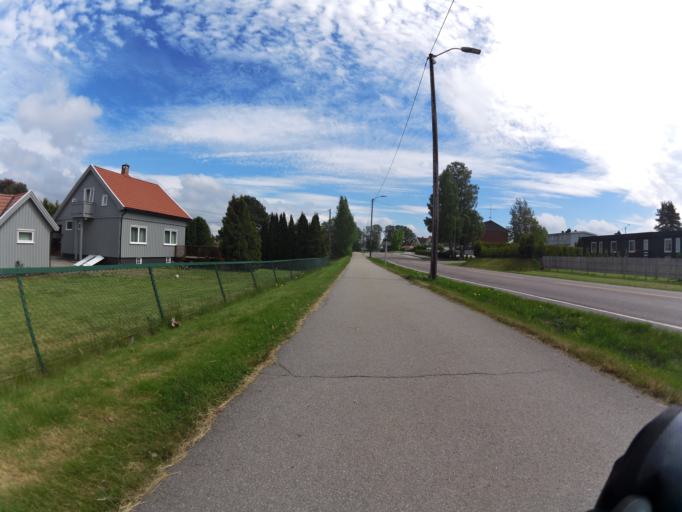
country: NO
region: Ostfold
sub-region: Rade
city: Karlshus
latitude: 59.3500
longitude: 10.8799
